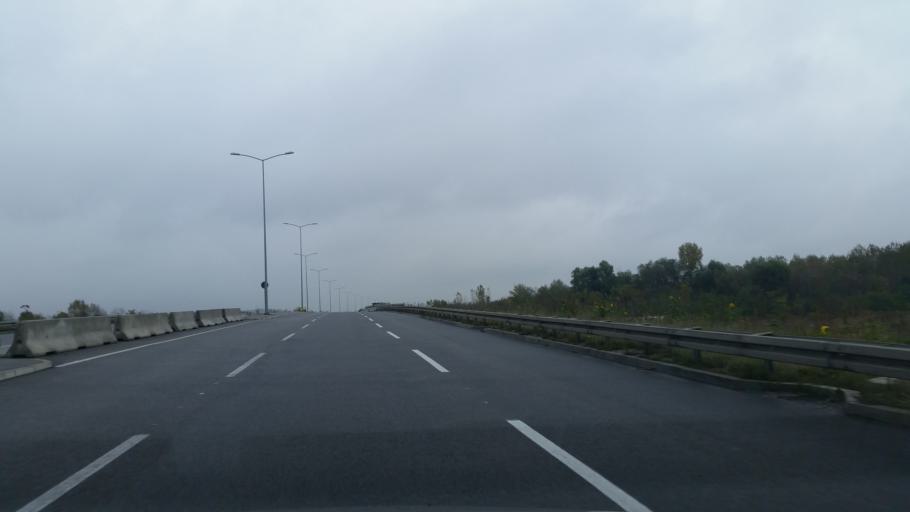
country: RS
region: Central Serbia
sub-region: Belgrade
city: Zemun
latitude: 44.8882
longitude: 20.4042
